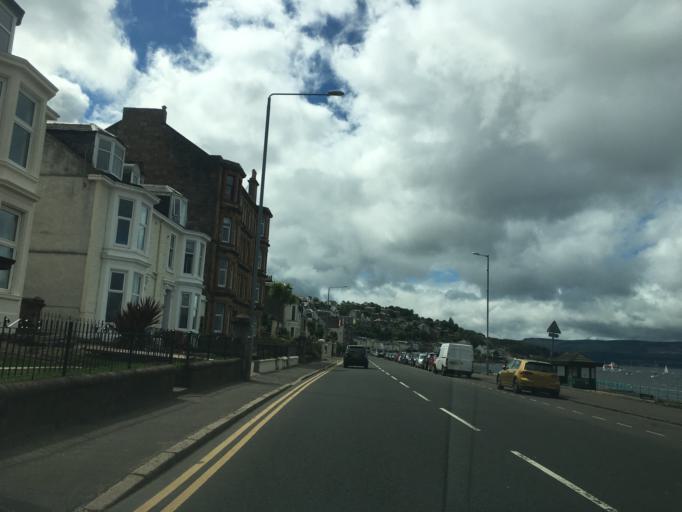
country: GB
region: Scotland
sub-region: Inverclyde
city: Gourock
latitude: 55.9583
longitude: -4.8252
